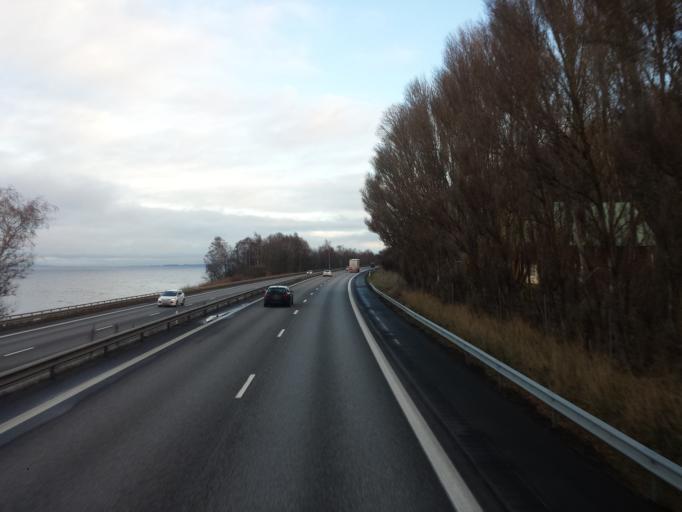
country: SE
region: Joenkoeping
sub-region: Jonkopings Kommun
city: Kaxholmen
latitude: 57.8780
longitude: 14.2771
